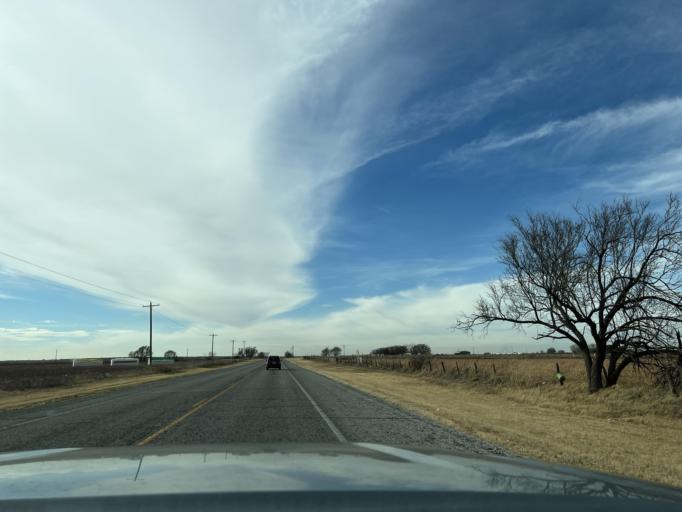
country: US
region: Texas
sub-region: Fisher County
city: Roby
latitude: 32.7583
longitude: -100.2839
